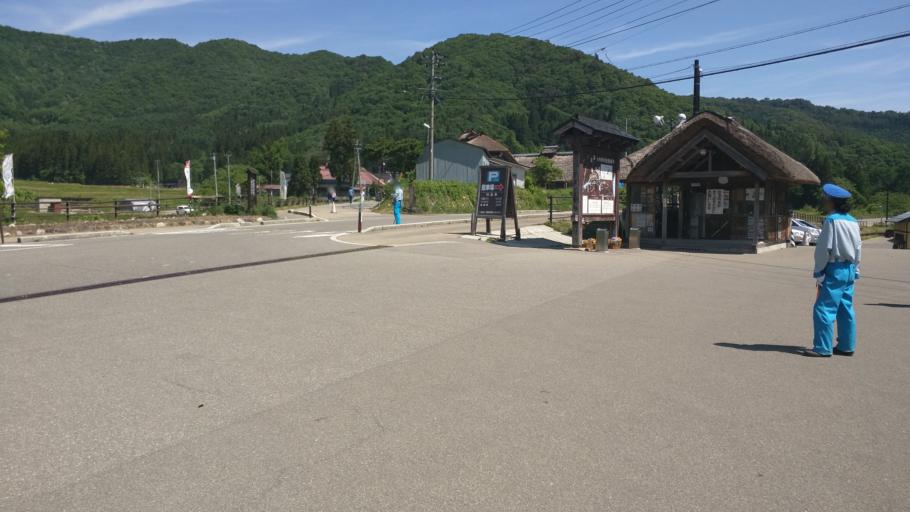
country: JP
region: Fukushima
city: Kitakata
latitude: 37.3306
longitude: 139.8606
